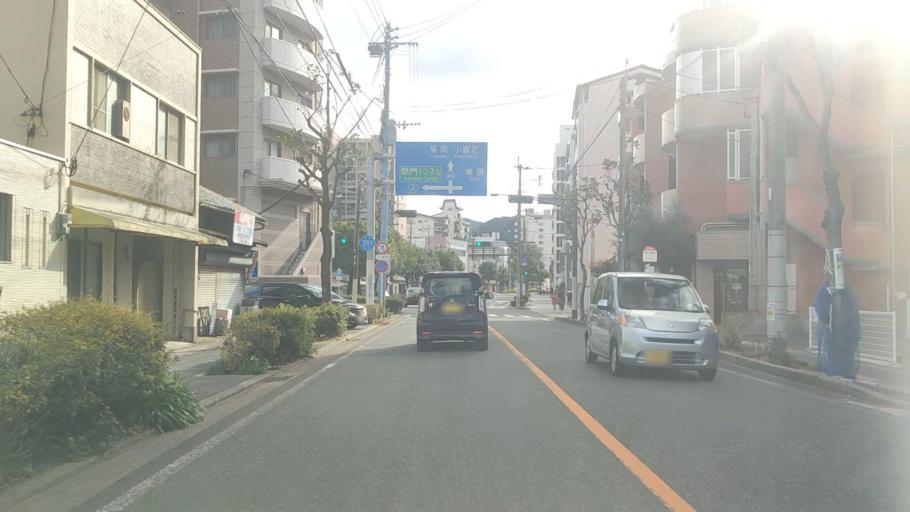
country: JP
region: Yamaguchi
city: Shimonoseki
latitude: 33.9525
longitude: 130.9671
